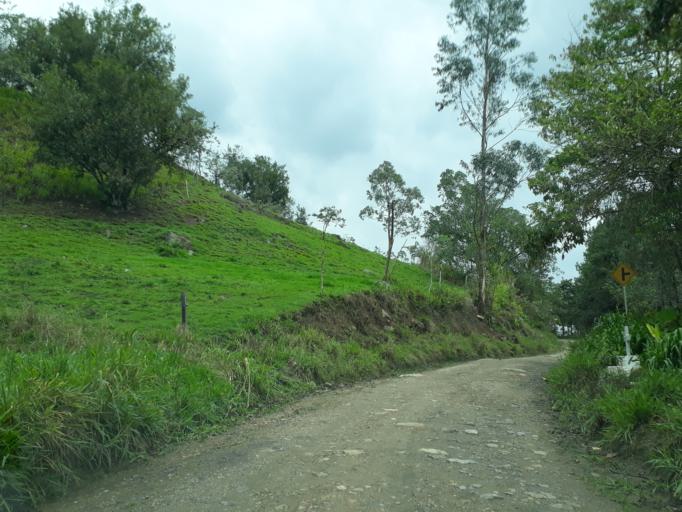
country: CO
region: Cundinamarca
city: Manta
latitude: 4.9855
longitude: -73.5575
